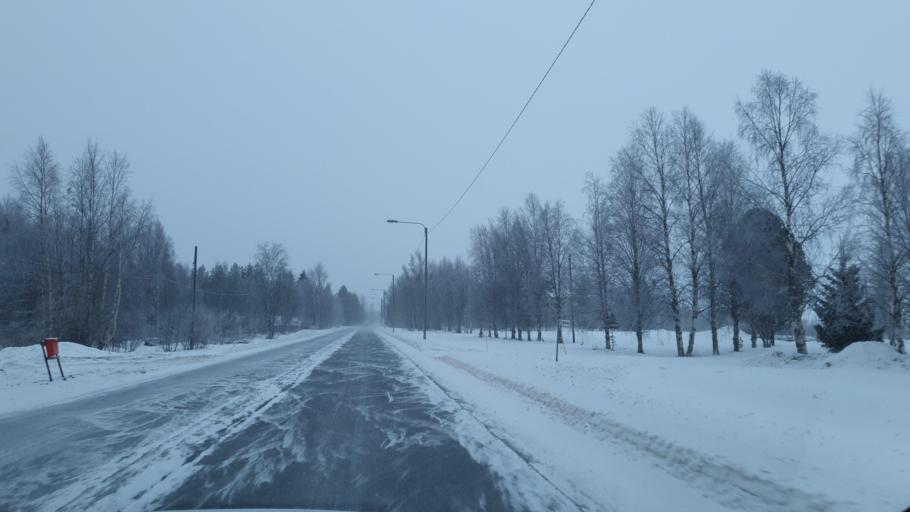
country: FI
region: Lapland
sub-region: Kemi-Tornio
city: Tornio
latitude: 66.0833
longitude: 23.9685
